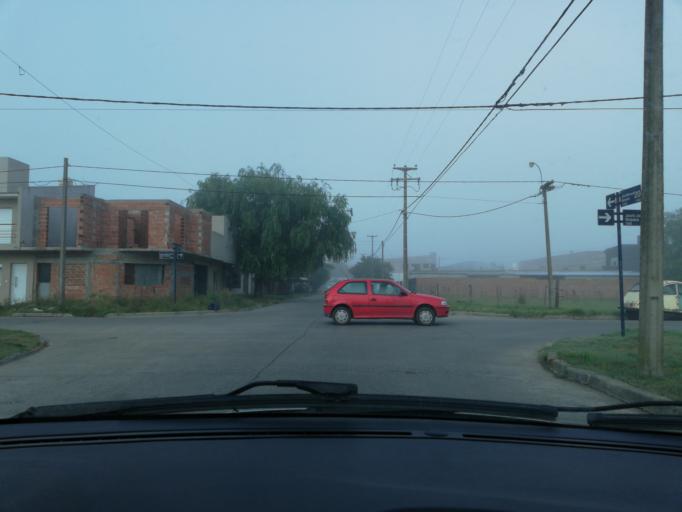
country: AR
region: Buenos Aires
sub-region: Partido de Balcarce
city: Balcarce
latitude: -37.8563
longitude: -58.2638
